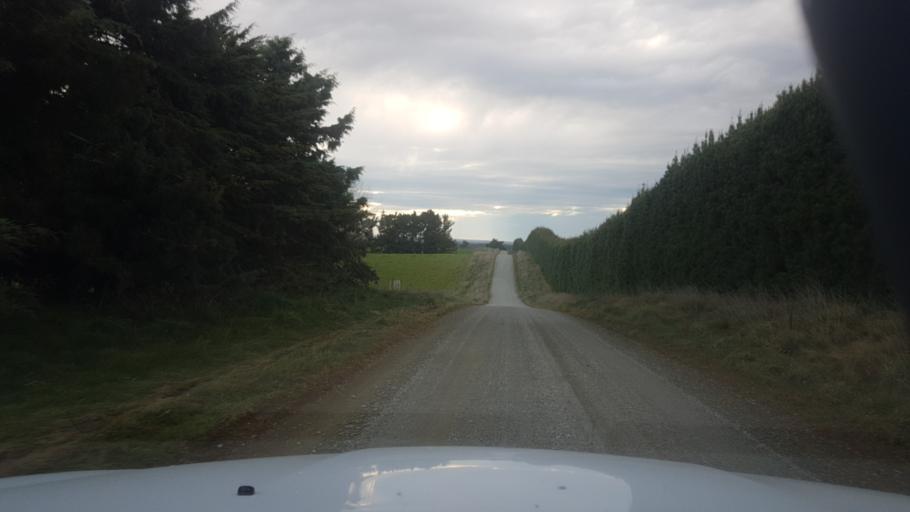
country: NZ
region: Canterbury
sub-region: Timaru District
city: Pleasant Point
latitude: -44.3423
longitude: 171.1410
